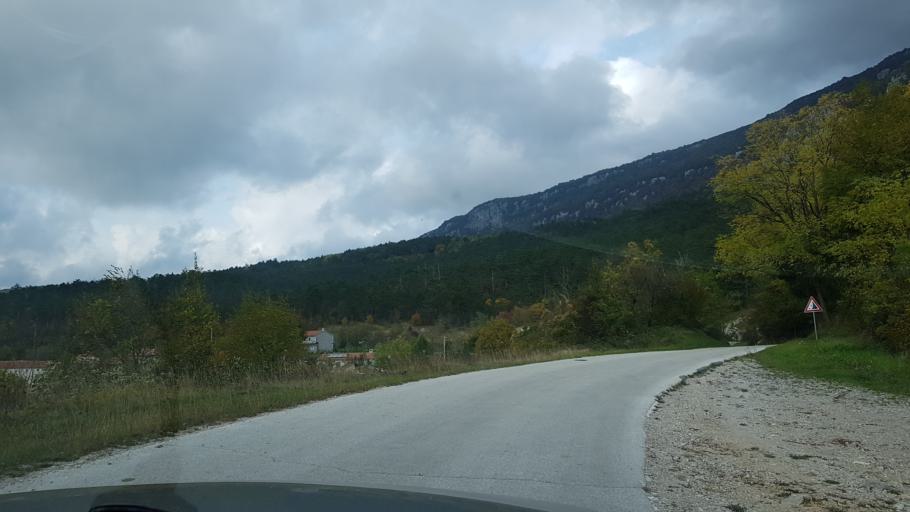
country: HR
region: Istarska
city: Buzet
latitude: 45.4074
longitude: 14.1185
